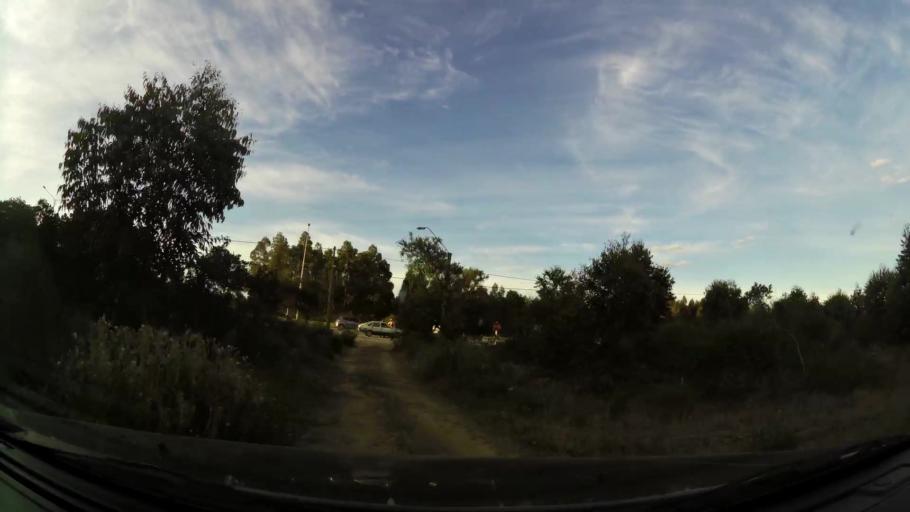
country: UY
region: Canelones
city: Atlantida
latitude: -34.7681
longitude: -55.7990
